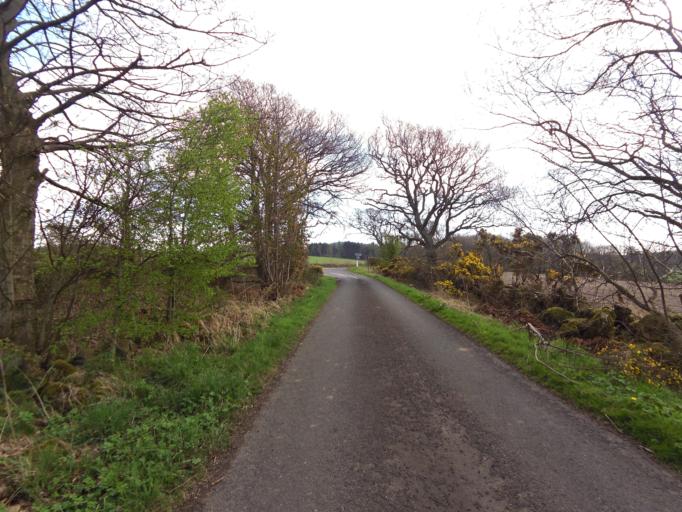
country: GB
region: Scotland
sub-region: Fife
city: Newburgh
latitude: 56.3311
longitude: -3.2308
